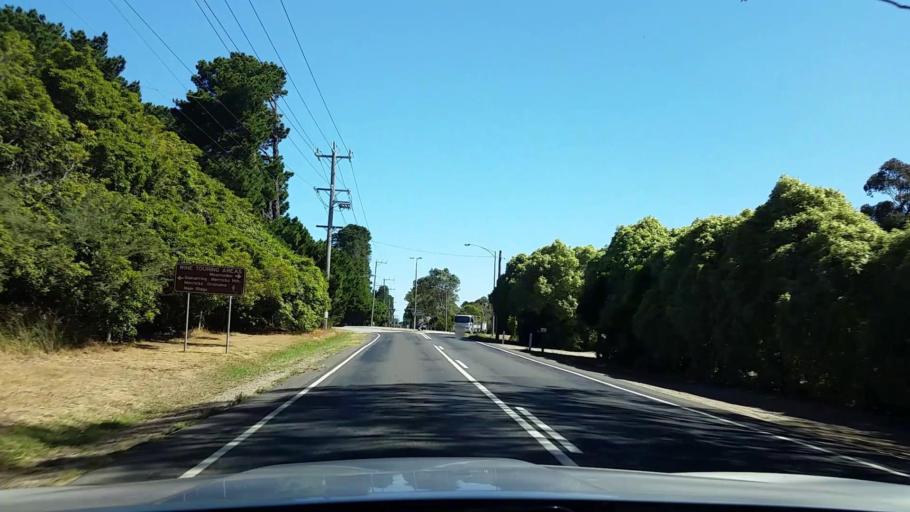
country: AU
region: Victoria
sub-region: Mornington Peninsula
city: Hastings
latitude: -38.2846
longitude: 145.1471
